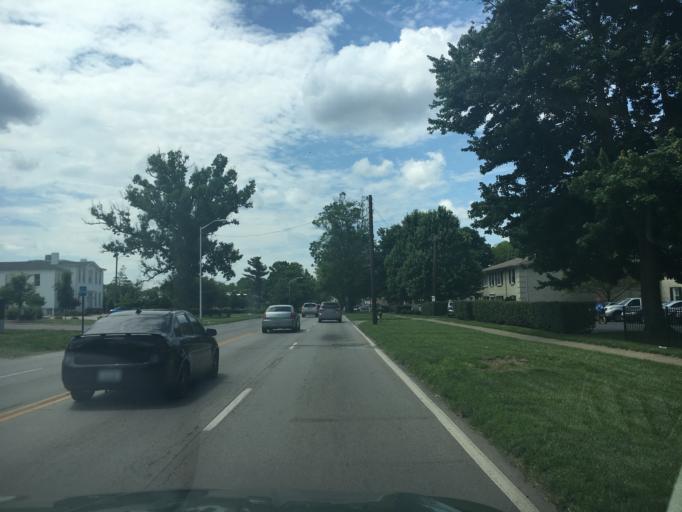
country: US
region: Kentucky
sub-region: Fayette County
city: Lexington-Fayette
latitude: 38.0618
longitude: -84.4815
